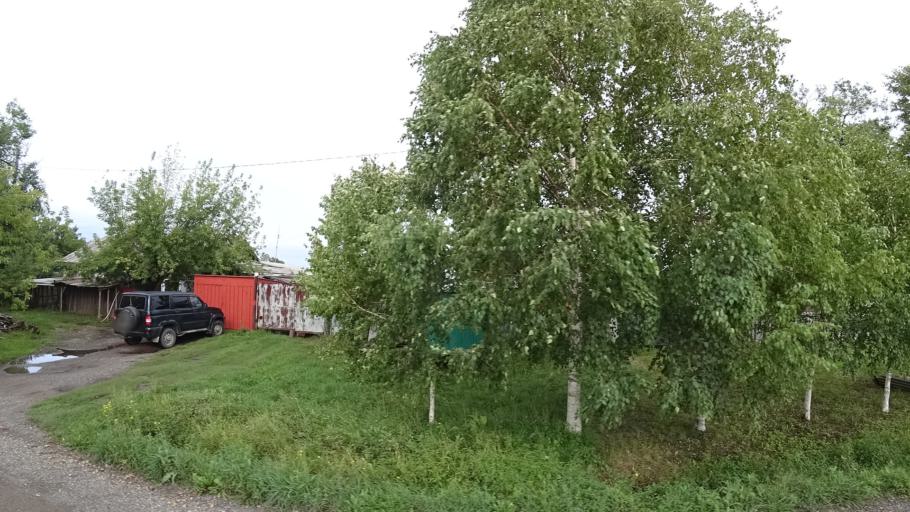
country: RU
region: Primorskiy
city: Chernigovka
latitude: 44.3353
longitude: 132.5777
